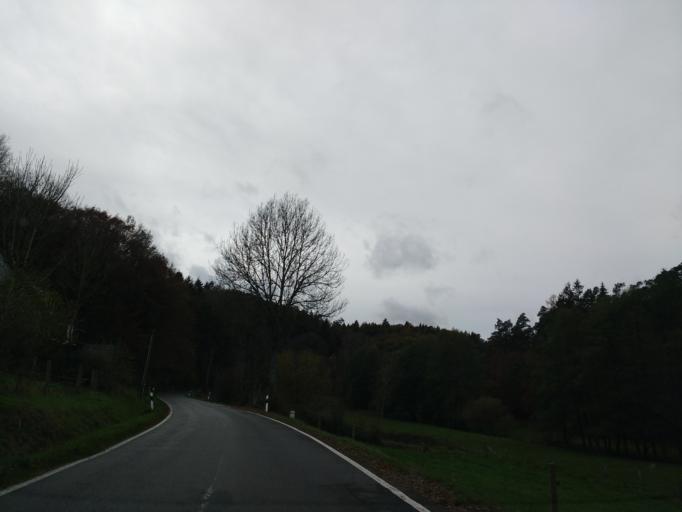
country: DE
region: Hesse
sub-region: Regierungsbezirk Kassel
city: Vohl
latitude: 51.1974
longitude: 8.9440
